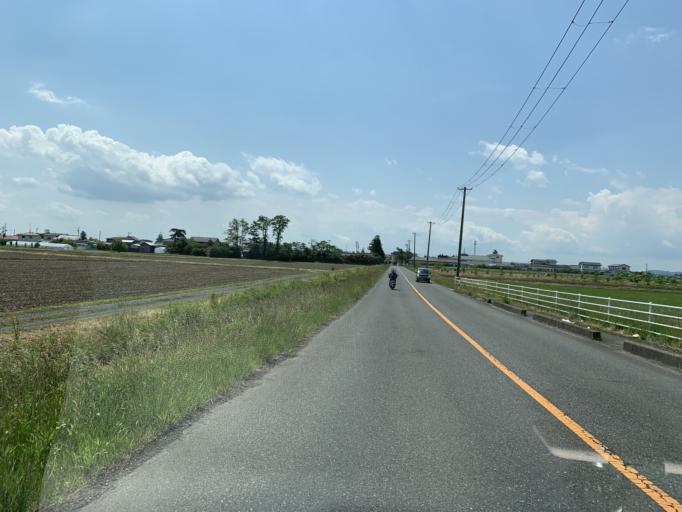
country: JP
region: Miyagi
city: Kogota
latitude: 38.5887
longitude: 141.0312
